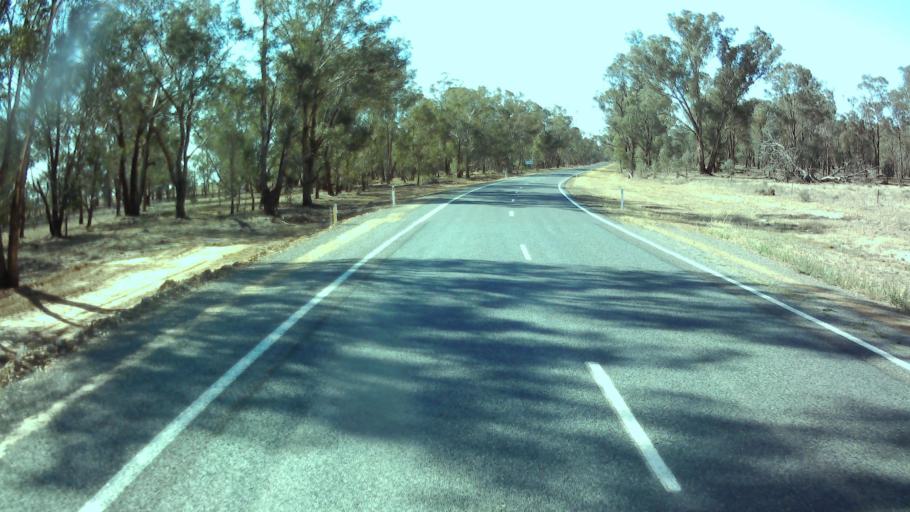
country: AU
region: New South Wales
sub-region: Weddin
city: Grenfell
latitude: -33.7205
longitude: 148.0812
